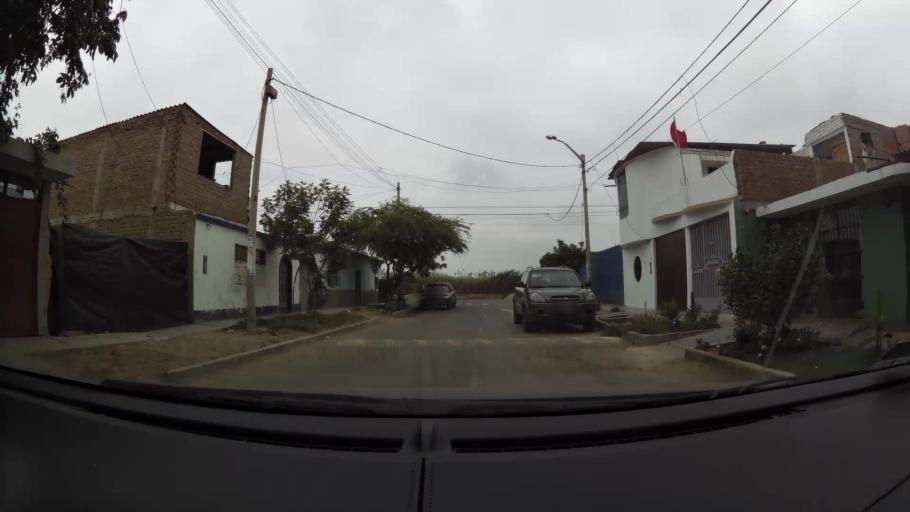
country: PE
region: La Libertad
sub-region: Provincia de Trujillo
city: Trujillo
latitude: -8.1197
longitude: -79.0464
